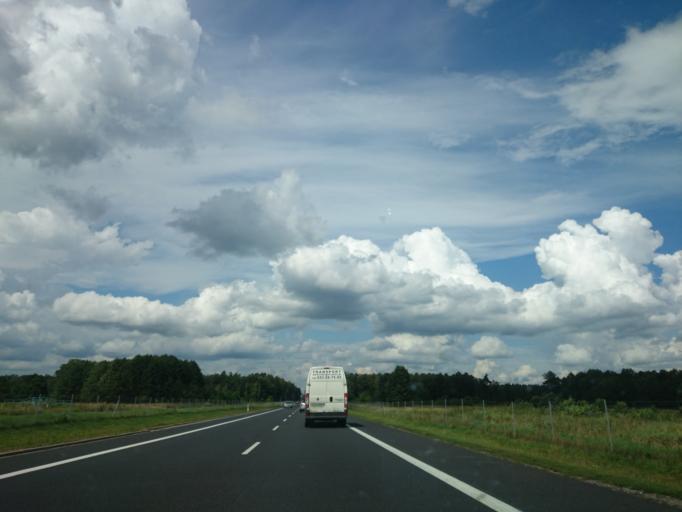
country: PL
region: Lubusz
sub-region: Powiat nowosolski
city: Otyn
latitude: 51.8445
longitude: 15.6728
